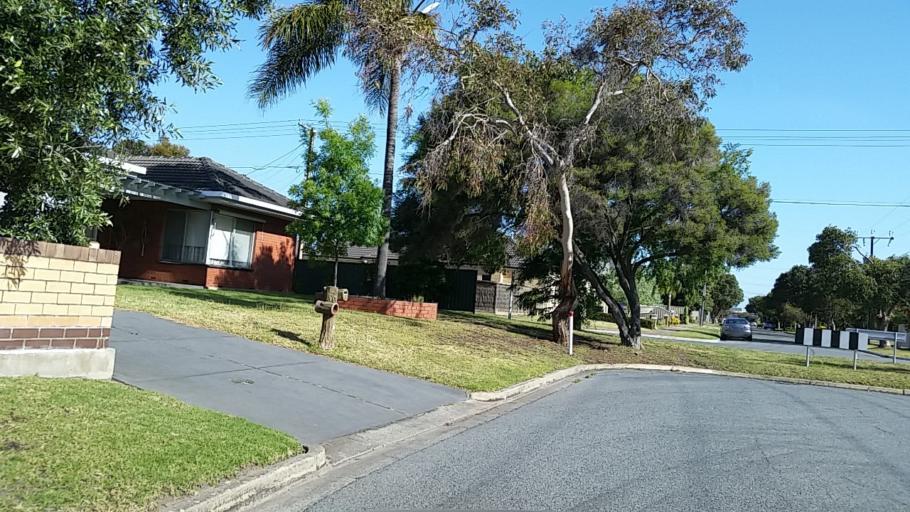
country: AU
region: South Australia
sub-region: Charles Sturt
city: Grange
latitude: -34.9094
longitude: 138.5019
